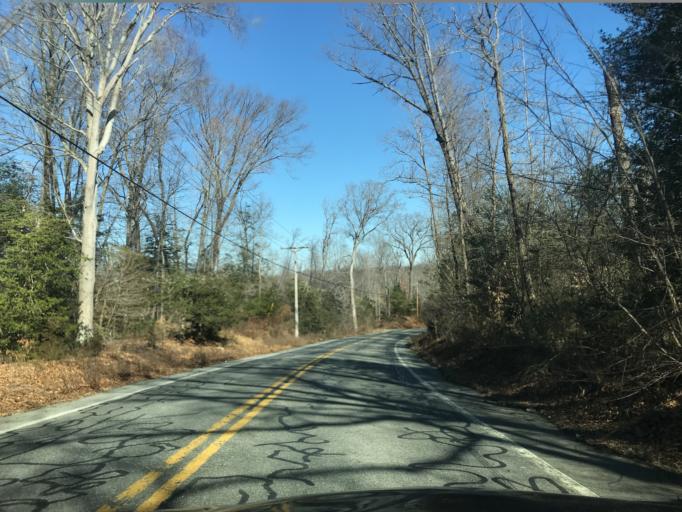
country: US
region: Virginia
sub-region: Prince William County
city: Cherry Hill
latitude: 38.5312
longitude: -77.2295
